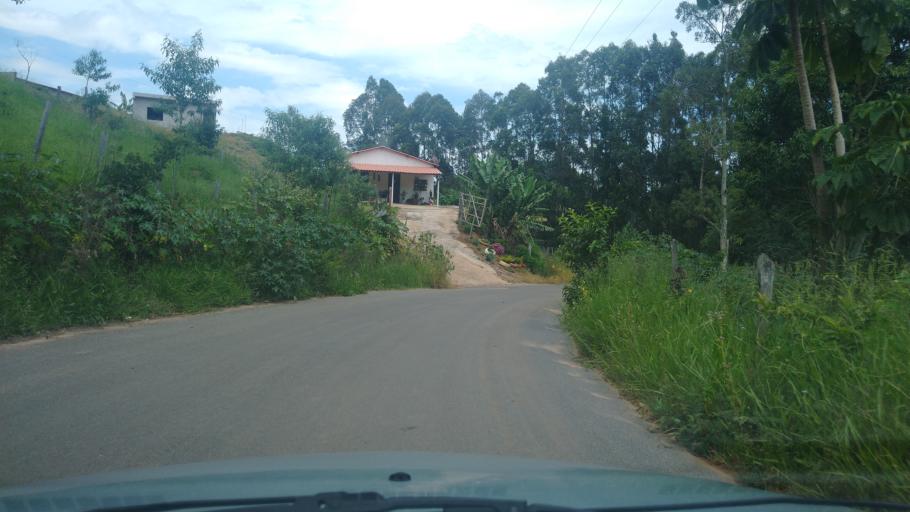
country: BR
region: Minas Gerais
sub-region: Extrema
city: Extrema
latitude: -22.7175
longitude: -46.3319
